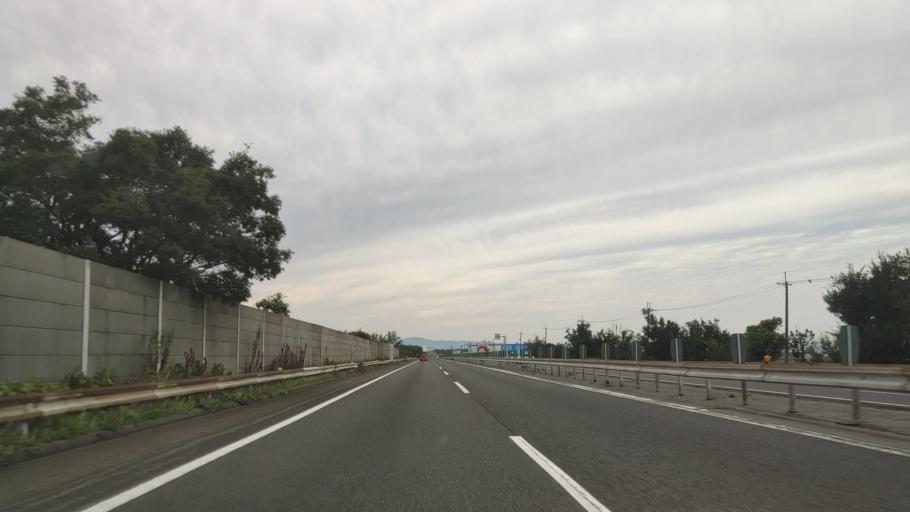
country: JP
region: Shiga Prefecture
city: Youkaichi
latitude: 35.1117
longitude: 136.2530
